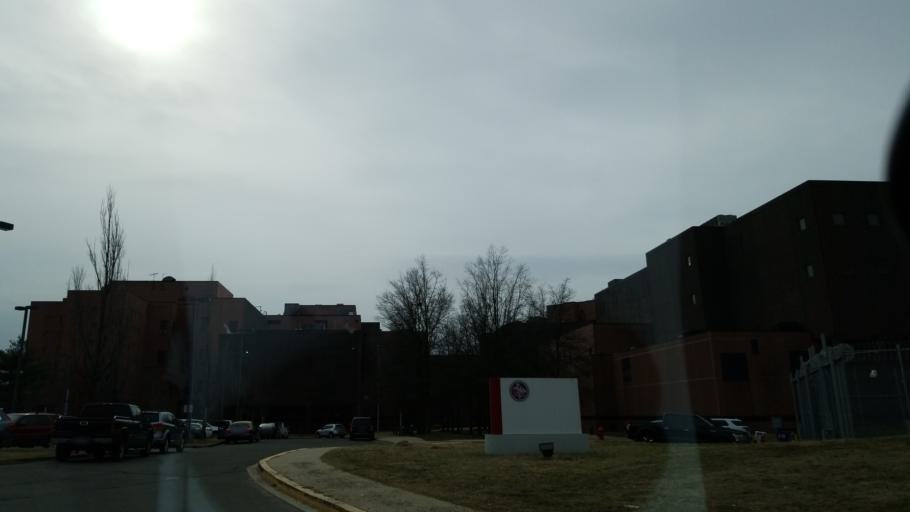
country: US
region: Maryland
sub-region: Prince George's County
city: Silver Hill
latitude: 38.8835
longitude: -76.9751
